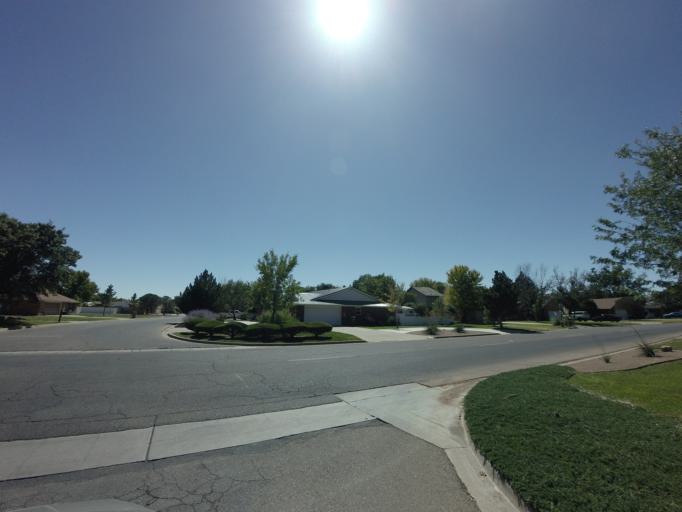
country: US
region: New Mexico
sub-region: Curry County
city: Clovis
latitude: 34.4405
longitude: -103.1809
